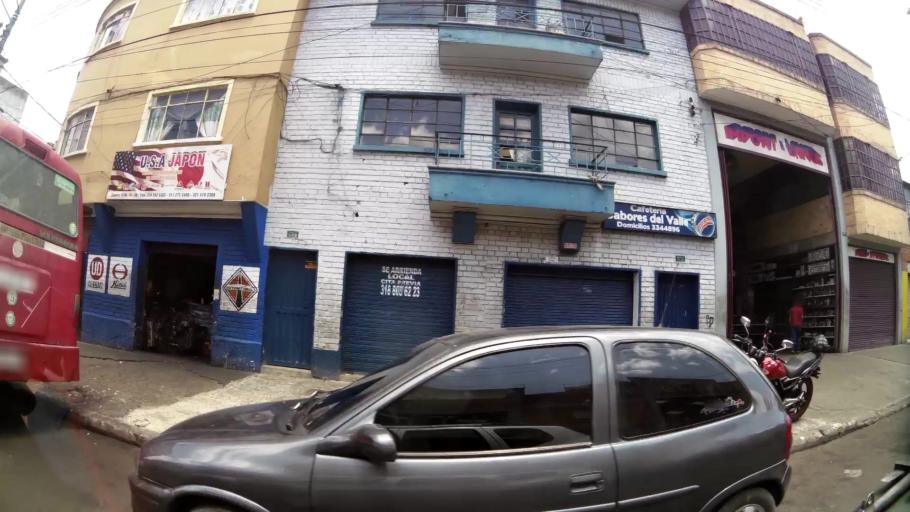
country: CO
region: Bogota D.C.
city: Bogota
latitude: 4.6004
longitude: -74.0855
